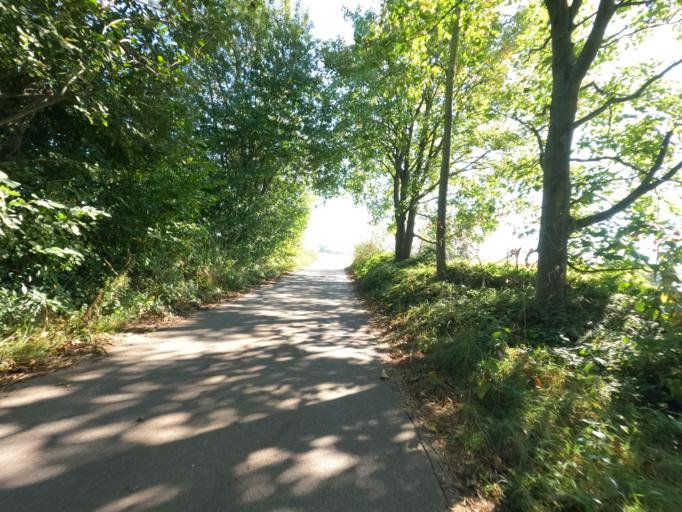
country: DE
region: North Rhine-Westphalia
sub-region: Regierungsbezirk Koln
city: Linnich
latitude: 50.9913
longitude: 6.2973
